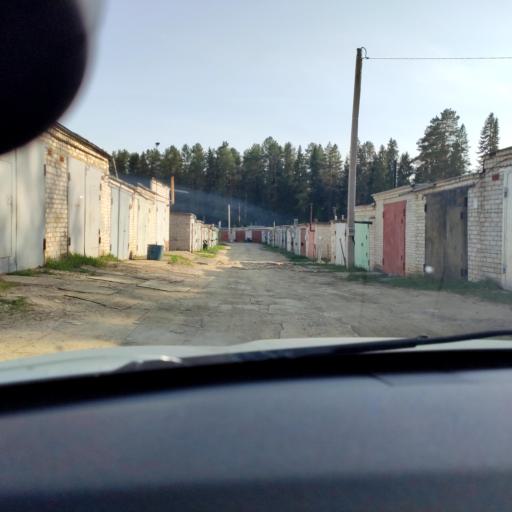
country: RU
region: Perm
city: Polazna
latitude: 58.2955
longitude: 56.3873
